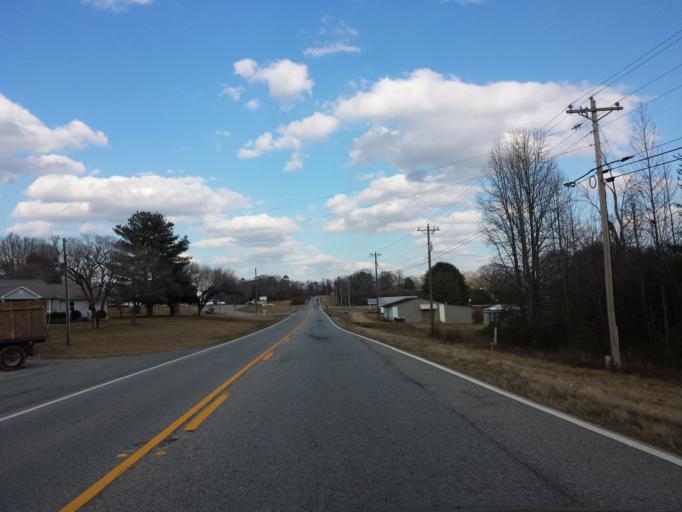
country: US
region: Georgia
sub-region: Lumpkin County
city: Dahlonega
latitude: 34.5321
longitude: -83.8664
